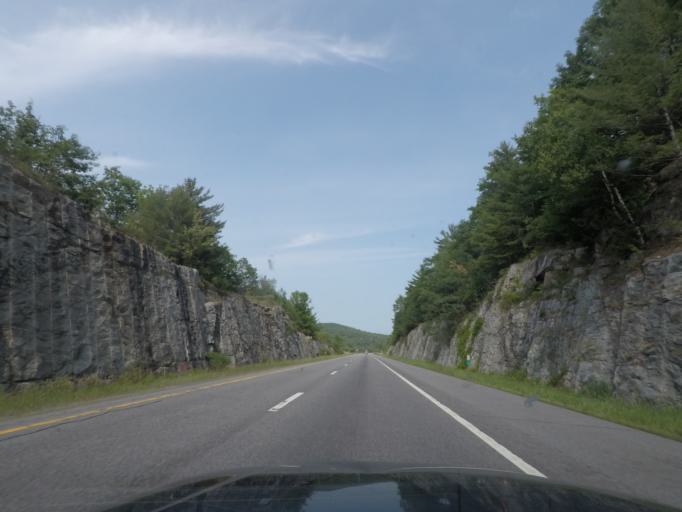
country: US
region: New York
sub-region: Essex County
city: Elizabethtown
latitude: 44.1935
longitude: -73.5397
